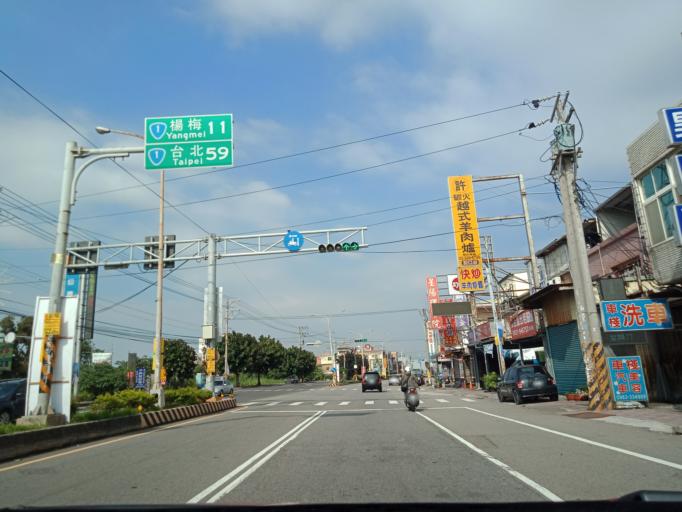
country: TW
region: Taiwan
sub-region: Hsinchu
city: Zhubei
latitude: 24.8796
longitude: 121.0071
